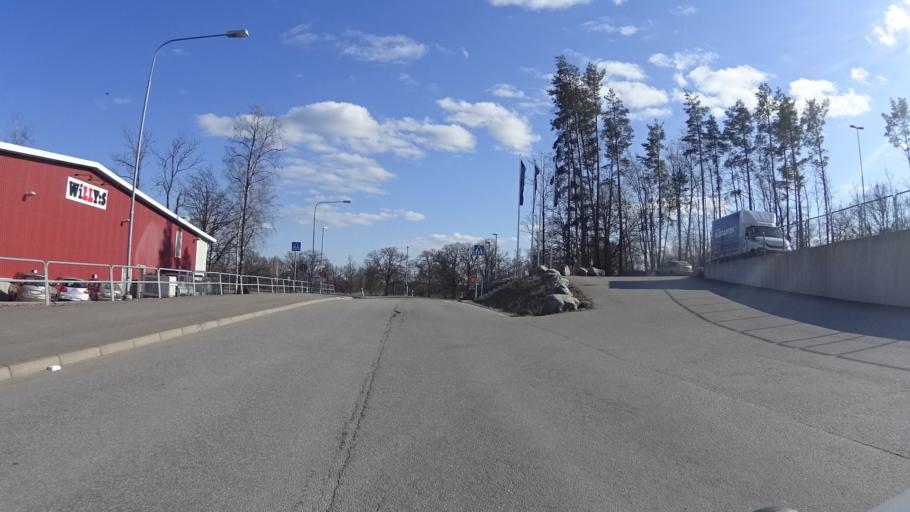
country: SE
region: Soedermanland
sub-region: Nykopings Kommun
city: Nykoping
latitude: 58.7472
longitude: 16.9719
